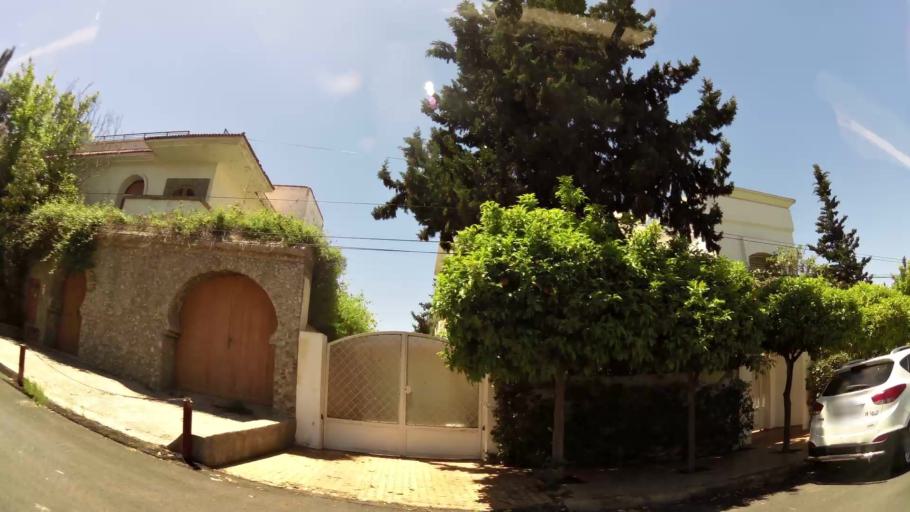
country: MA
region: Meknes-Tafilalet
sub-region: Meknes
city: Meknes
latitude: 33.9101
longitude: -5.5498
